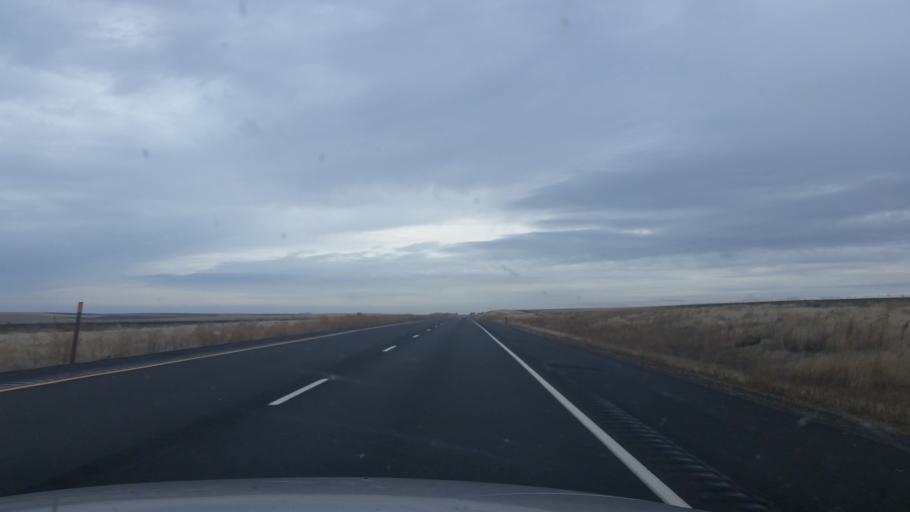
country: US
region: Washington
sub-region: Grant County
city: Warden
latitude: 47.0865
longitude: -118.7747
